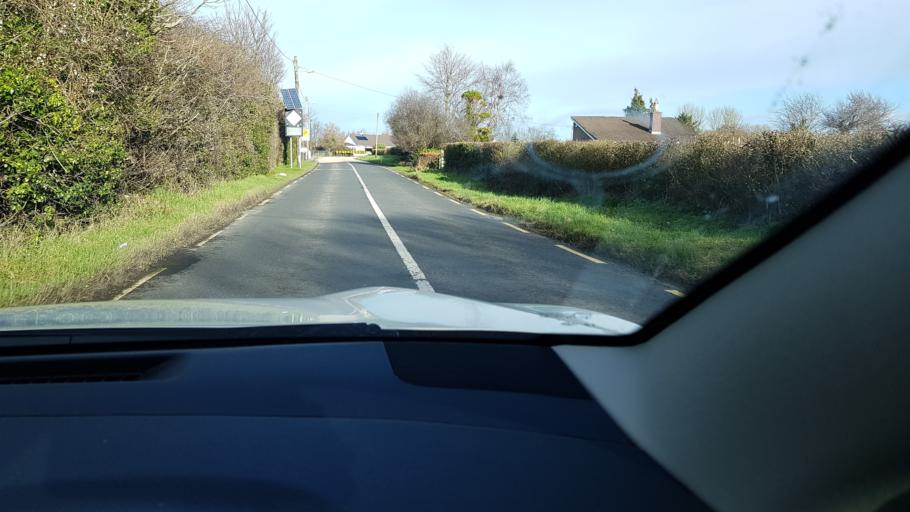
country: IE
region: Leinster
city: Lucan
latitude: 53.3719
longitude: -6.4549
